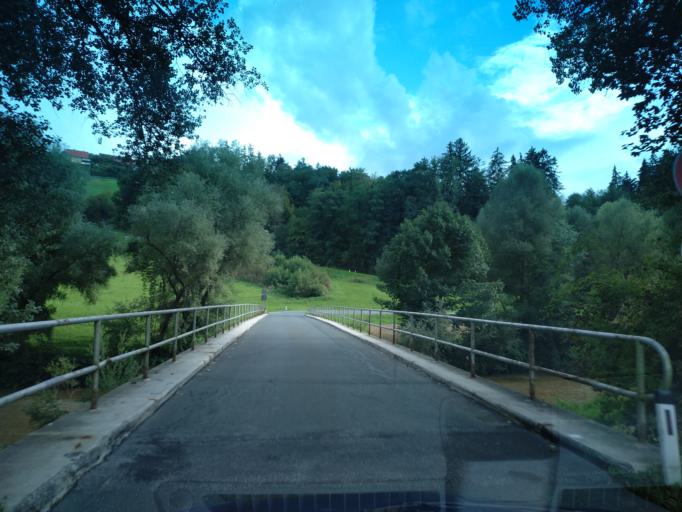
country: AT
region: Styria
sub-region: Politischer Bezirk Leibnitz
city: Seggauberg
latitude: 46.7774
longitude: 15.5194
